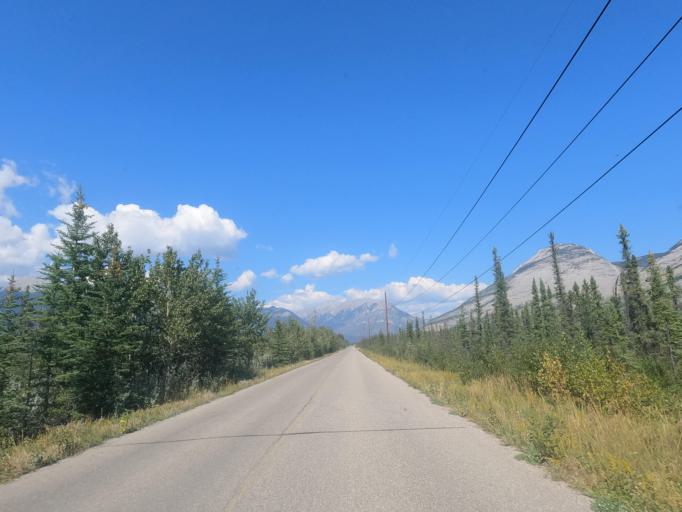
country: CA
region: Alberta
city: Jasper Park Lodge
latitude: 53.0029
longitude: -118.0852
